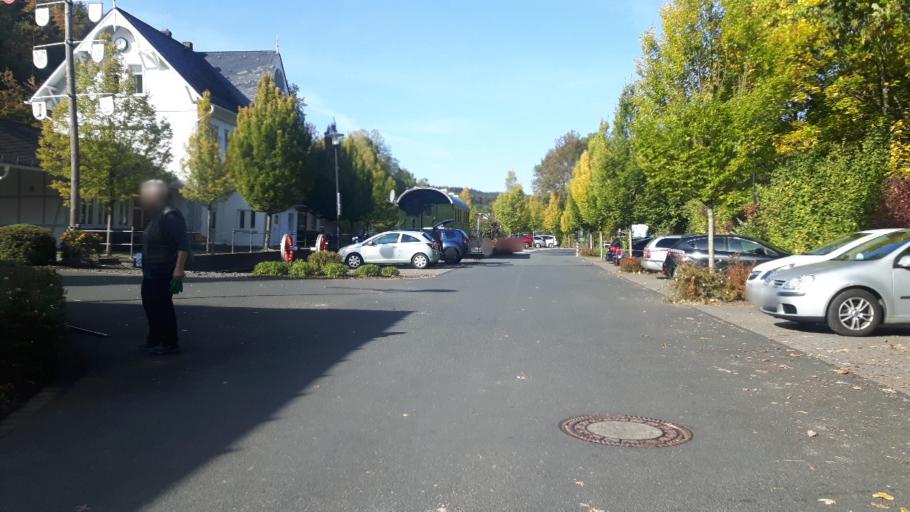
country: DE
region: North Rhine-Westphalia
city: Netphen
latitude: 50.8812
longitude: 8.1436
